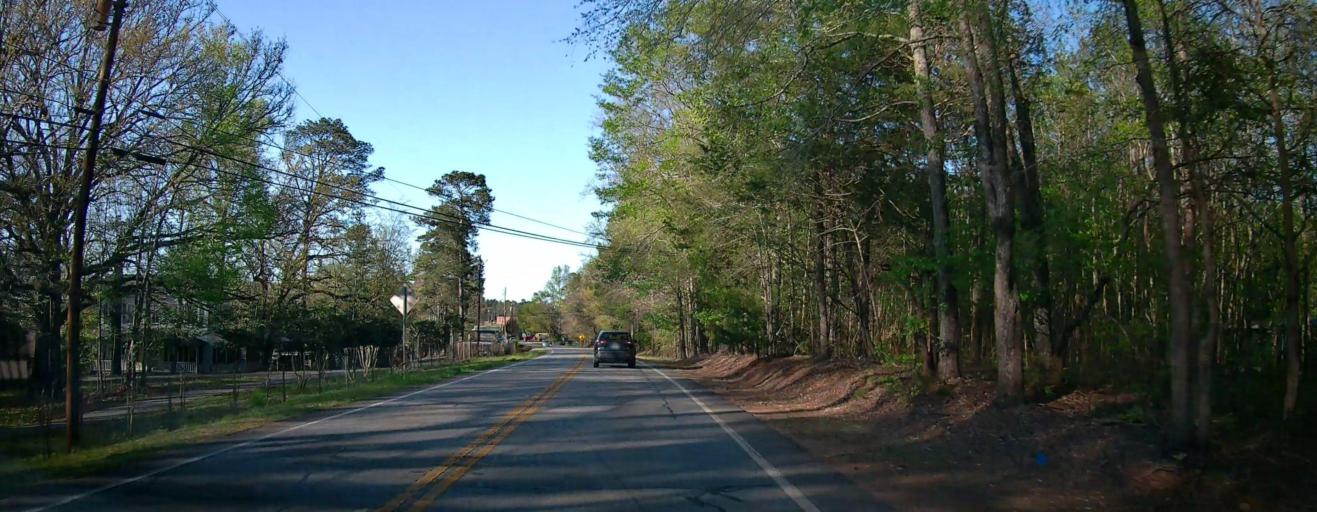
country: US
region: Georgia
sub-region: Butts County
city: Indian Springs
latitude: 33.2593
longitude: -83.9098
